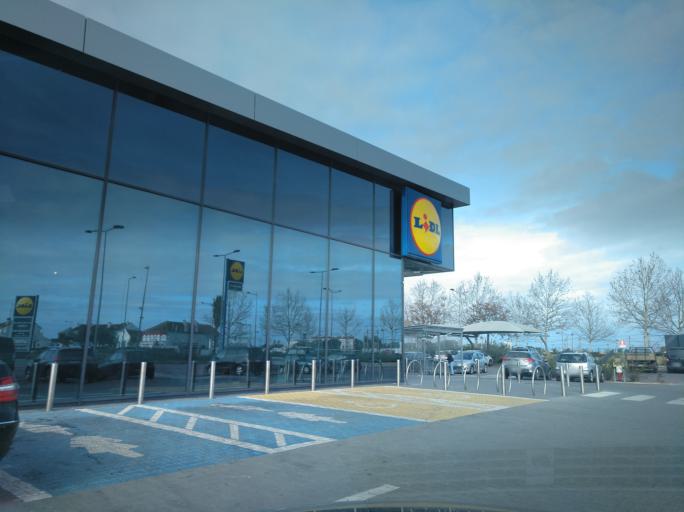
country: PT
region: Setubal
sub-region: Grandola
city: Grandola
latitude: 38.1847
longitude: -8.5687
